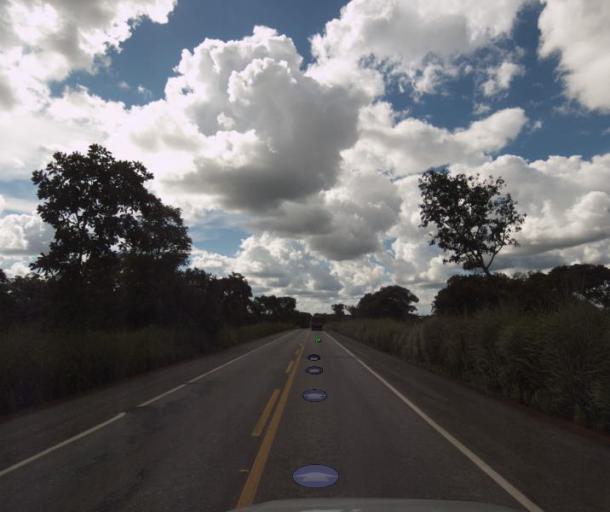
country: BR
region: Goias
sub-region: Porangatu
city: Porangatu
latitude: -13.3059
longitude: -49.1195
